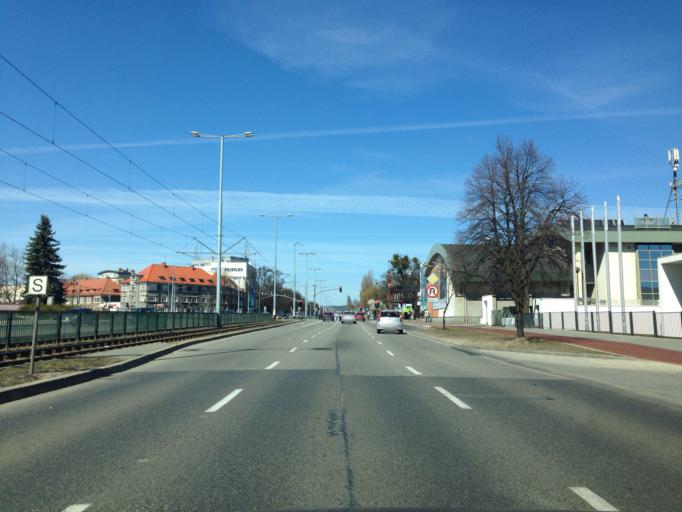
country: PL
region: Pomeranian Voivodeship
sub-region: Gdansk
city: Gdansk
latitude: 54.3862
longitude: 18.5928
